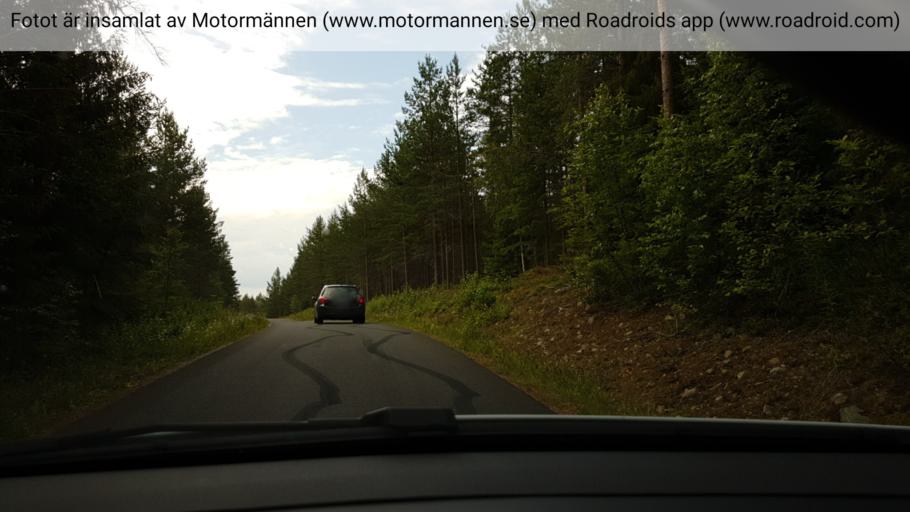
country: SE
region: Dalarna
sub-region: Rattviks Kommun
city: Raettvik
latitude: 61.0107
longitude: 15.1958
